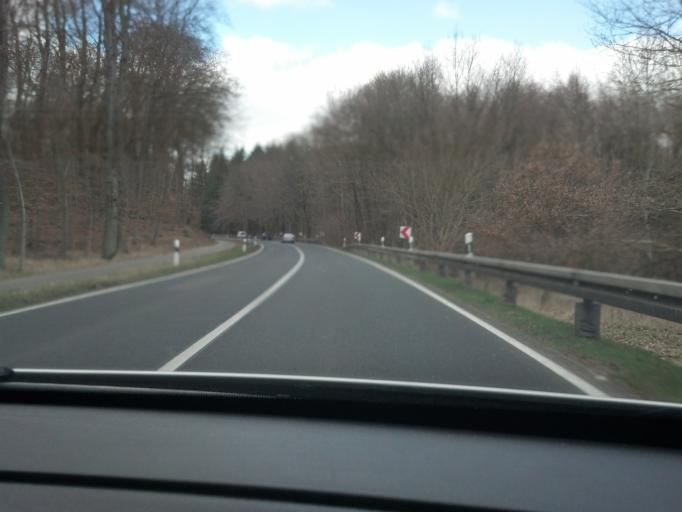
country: DE
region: Mecklenburg-Vorpommern
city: Carpin
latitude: 53.3576
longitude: 13.2254
